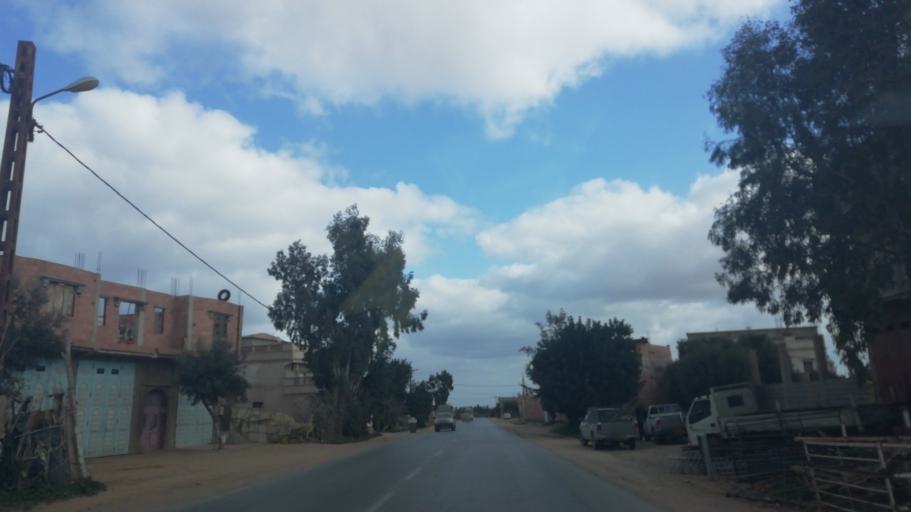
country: DZ
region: Relizane
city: Mazouna
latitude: 36.2753
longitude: 0.6353
